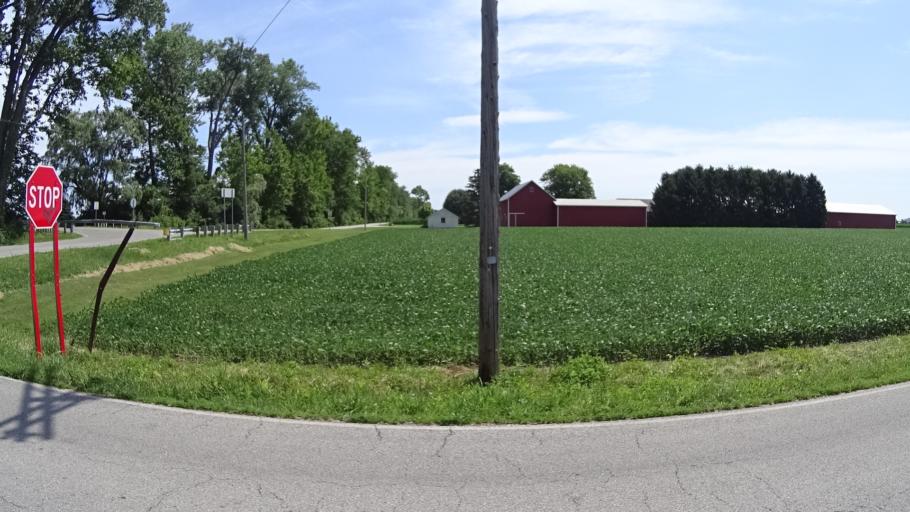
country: US
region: Ohio
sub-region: Erie County
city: Sandusky
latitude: 41.4229
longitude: -82.7921
